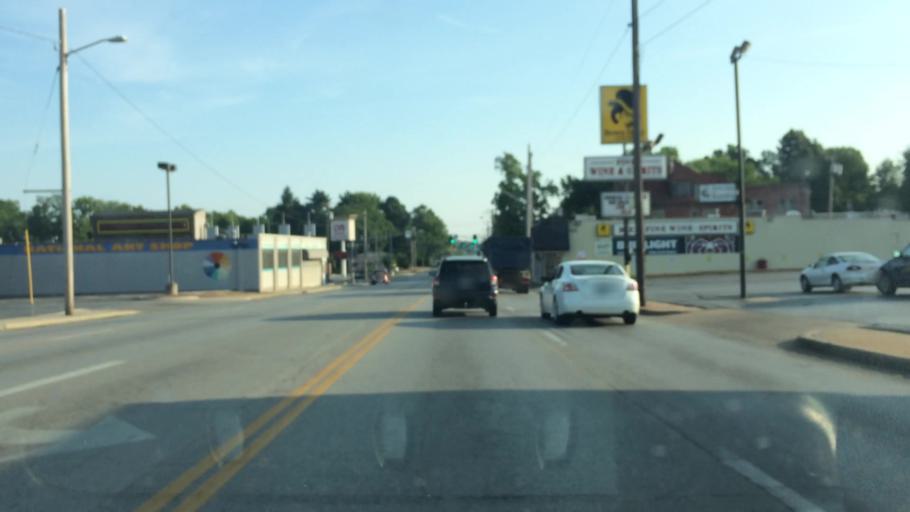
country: US
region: Missouri
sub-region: Greene County
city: Springfield
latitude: 37.2041
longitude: -93.2761
